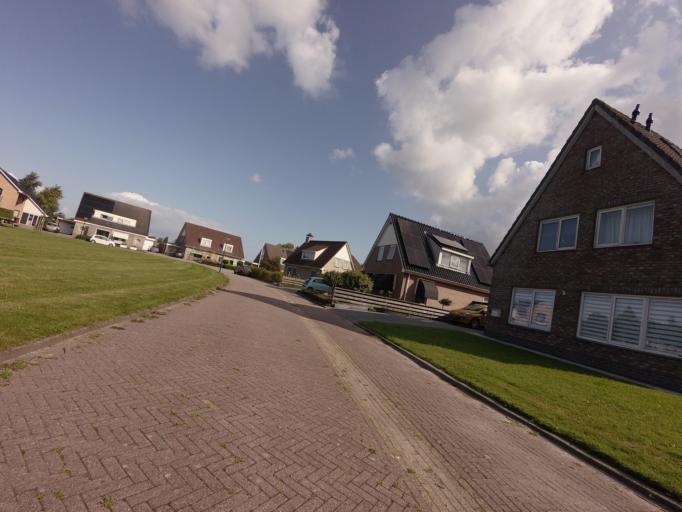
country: NL
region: Friesland
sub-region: Gemeente Franekeradeel
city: Tzummarum
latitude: 53.2377
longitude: 5.5434
